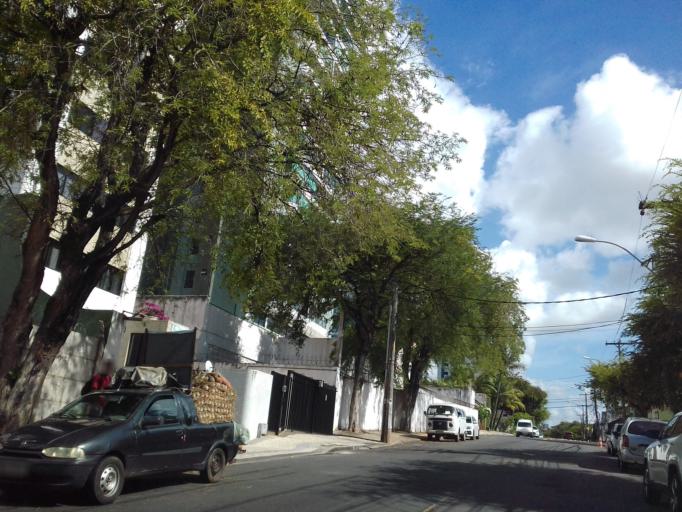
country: BR
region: Bahia
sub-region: Salvador
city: Salvador
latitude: -12.9840
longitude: -38.4605
